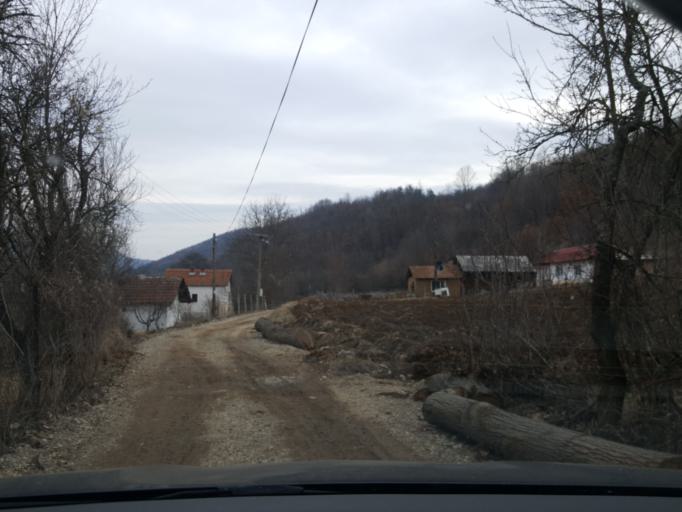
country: RS
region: Central Serbia
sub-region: Pirotski Okrug
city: Dimitrovgrad
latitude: 43.0039
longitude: 22.7581
